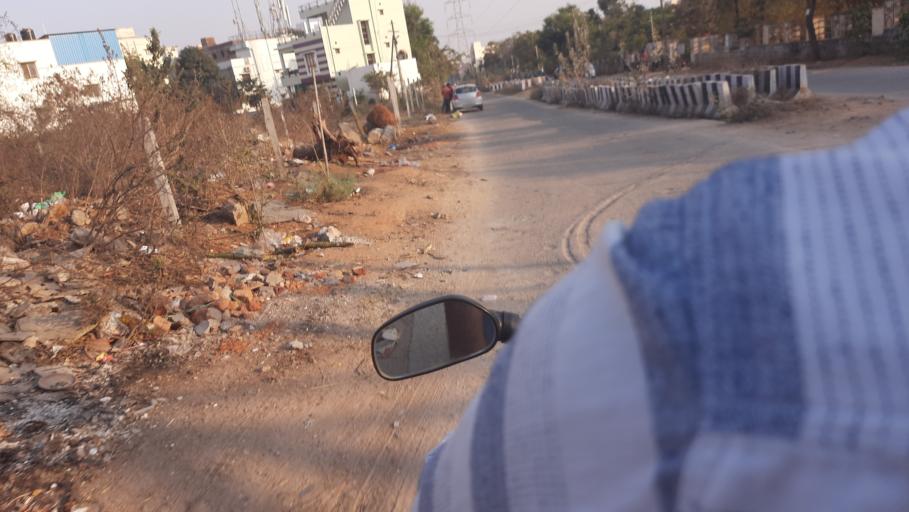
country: IN
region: Telangana
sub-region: Rangareddi
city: Secunderabad
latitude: 17.5012
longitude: 78.5391
